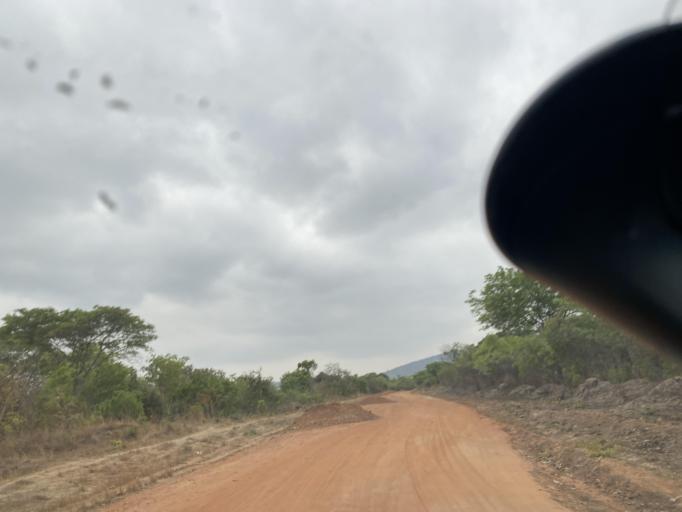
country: ZM
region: Lusaka
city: Chongwe
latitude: -15.2051
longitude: 28.7612
